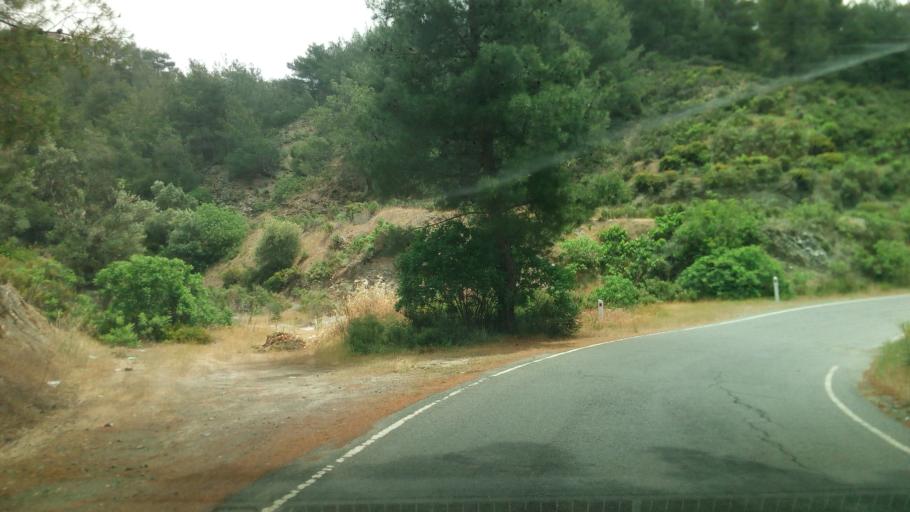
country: CY
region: Limassol
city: Pelendri
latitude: 34.8969
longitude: 32.9958
